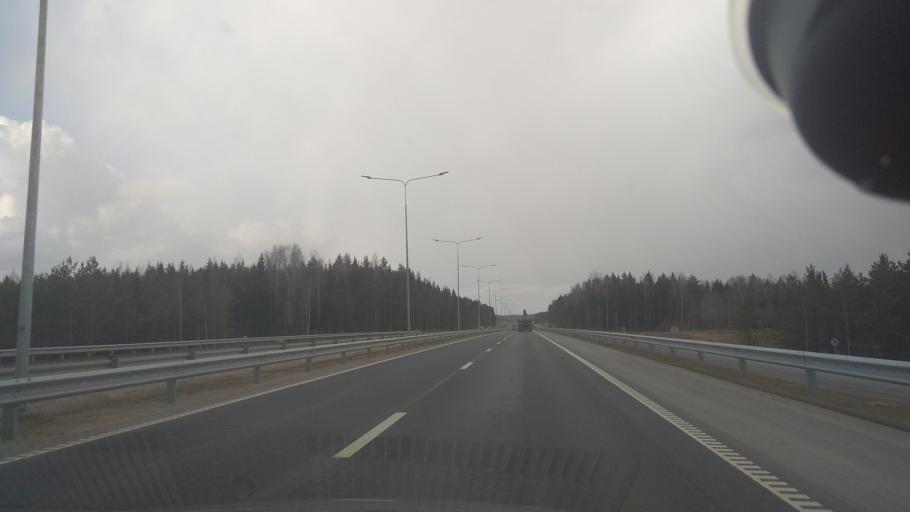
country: LT
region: Vilnius County
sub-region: Vilnius
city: Fabijoniskes
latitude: 54.8488
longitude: 25.2877
